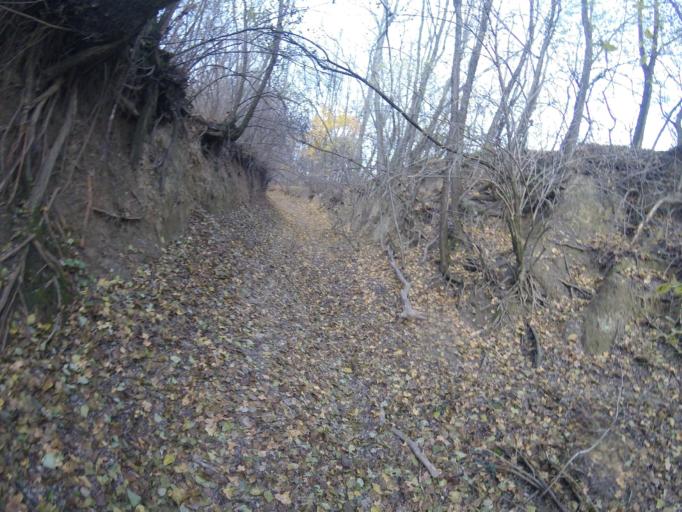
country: HU
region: Tolna
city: Szentgalpuszta
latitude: 46.3424
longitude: 18.6444
